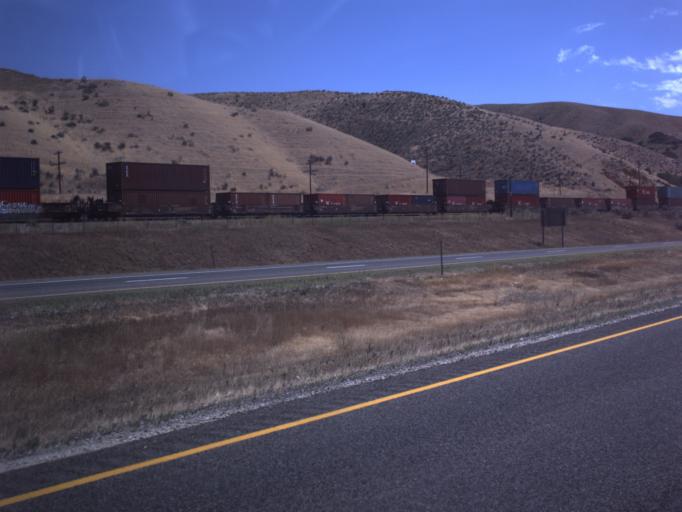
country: US
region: Utah
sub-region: Summit County
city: Coalville
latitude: 41.0079
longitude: -111.4786
